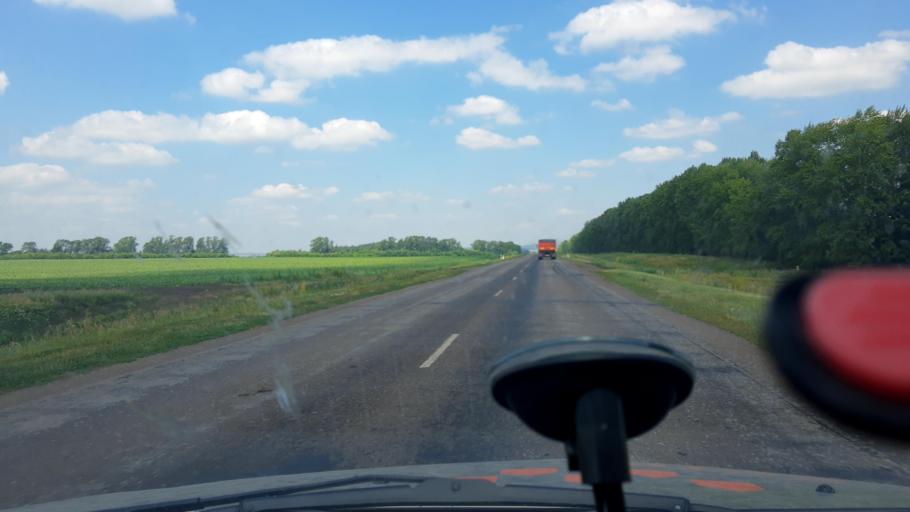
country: RU
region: Bashkortostan
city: Buzdyak
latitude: 54.8507
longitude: 54.5666
